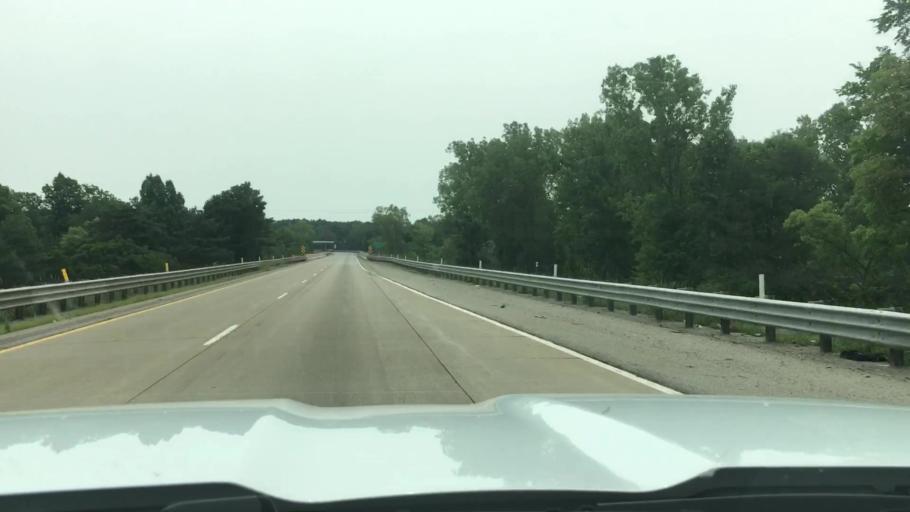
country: US
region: Michigan
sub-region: Eaton County
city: Dimondale
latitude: 42.6712
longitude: -84.6474
